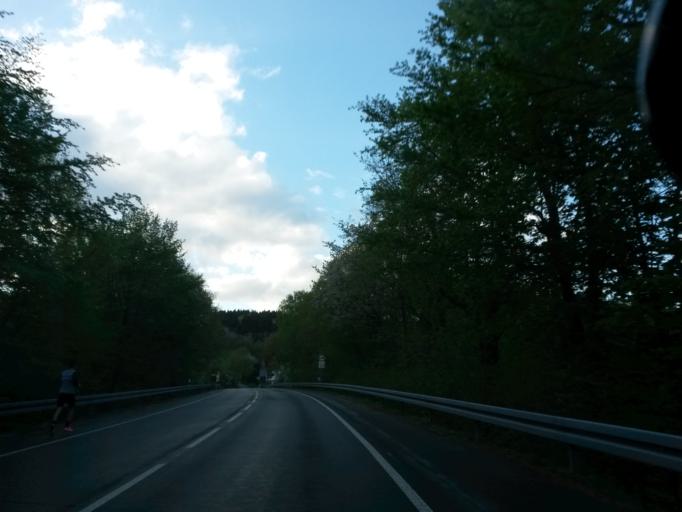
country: DE
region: North Rhine-Westphalia
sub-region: Regierungsbezirk Arnsberg
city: Herscheid
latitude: 51.1569
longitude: 7.7437
